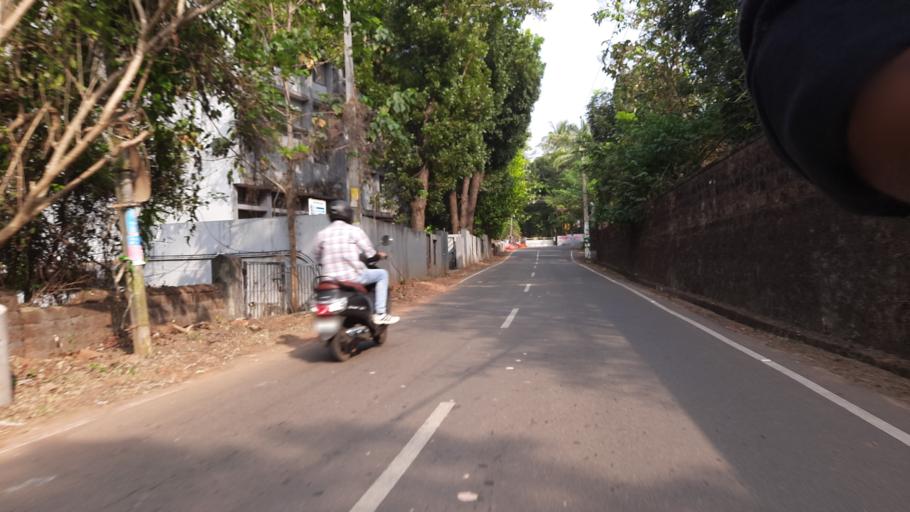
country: IN
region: Kerala
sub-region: Kozhikode
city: Ferokh
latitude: 11.1994
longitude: 75.8582
